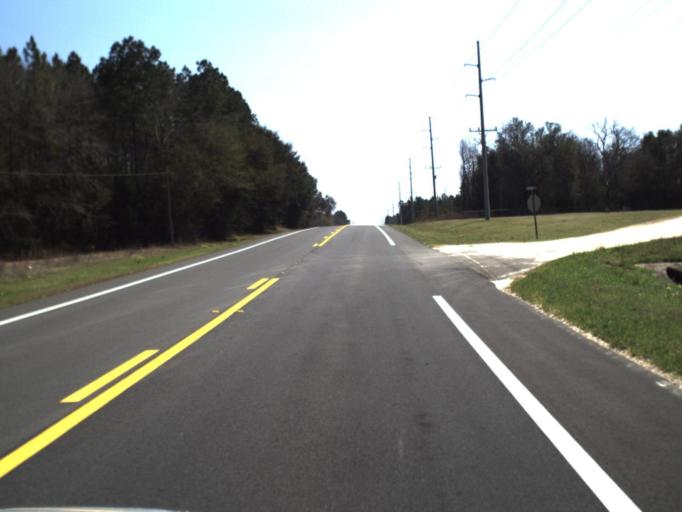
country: US
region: Florida
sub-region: Jackson County
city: Sneads
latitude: 30.8015
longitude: -85.0321
